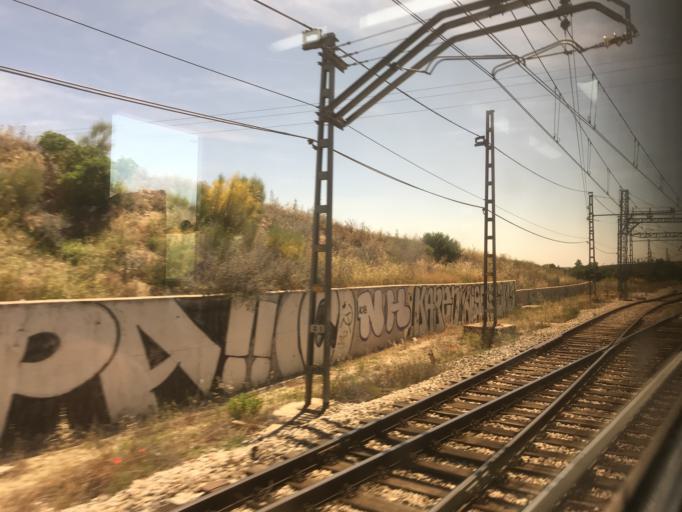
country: ES
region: Madrid
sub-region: Provincia de Madrid
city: Valdemoro
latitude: 40.2001
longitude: -3.6674
